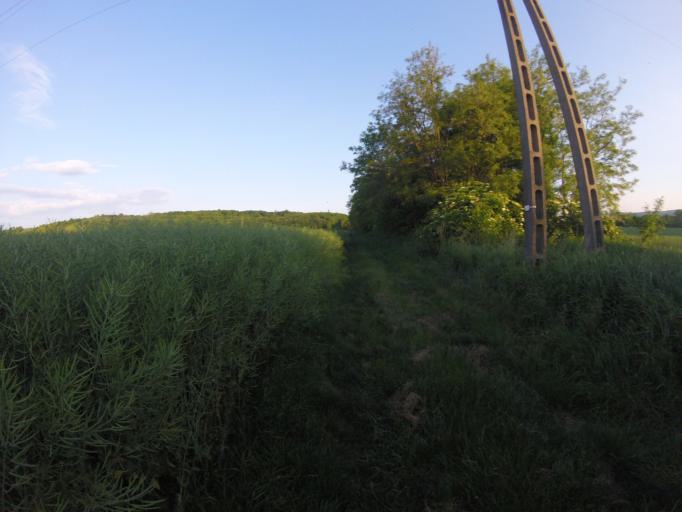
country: HU
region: Zala
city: Zalaszentgrot
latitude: 46.8732
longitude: 17.1184
